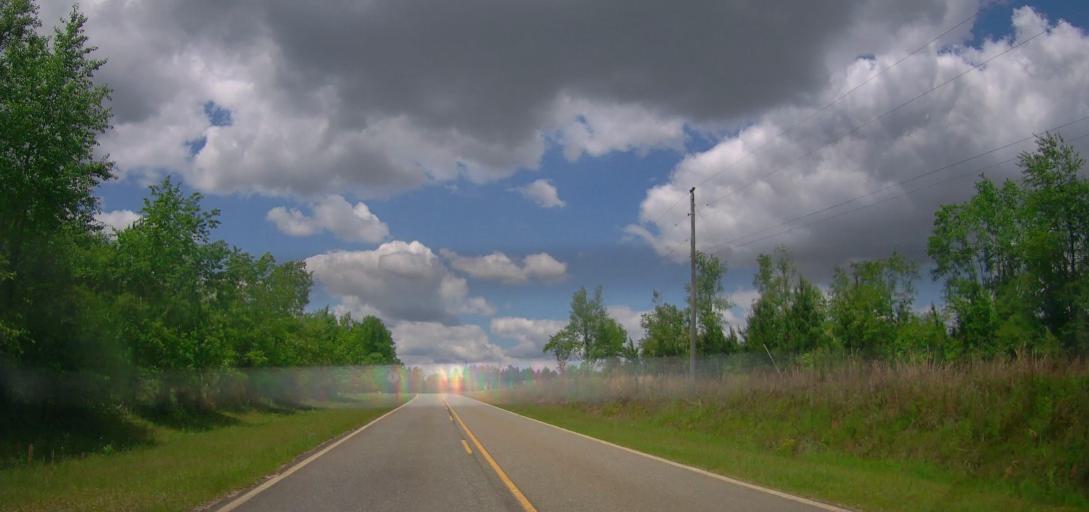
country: US
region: Georgia
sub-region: Laurens County
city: East Dublin
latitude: 32.6013
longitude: -82.8005
